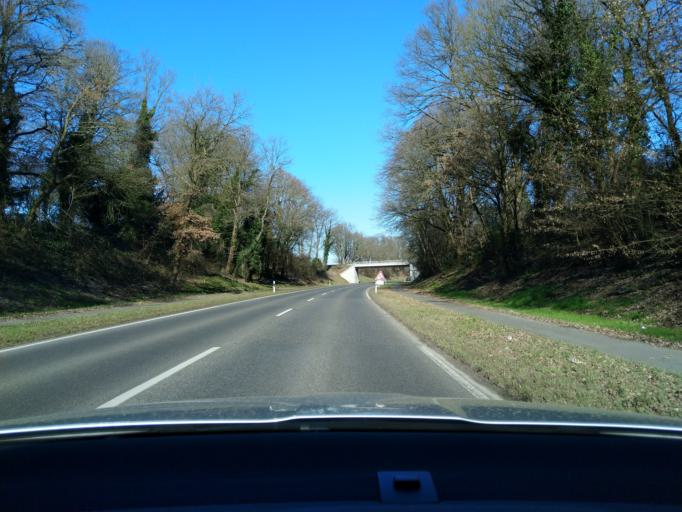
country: DE
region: North Rhine-Westphalia
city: Wegberg
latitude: 51.1440
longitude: 6.2671
